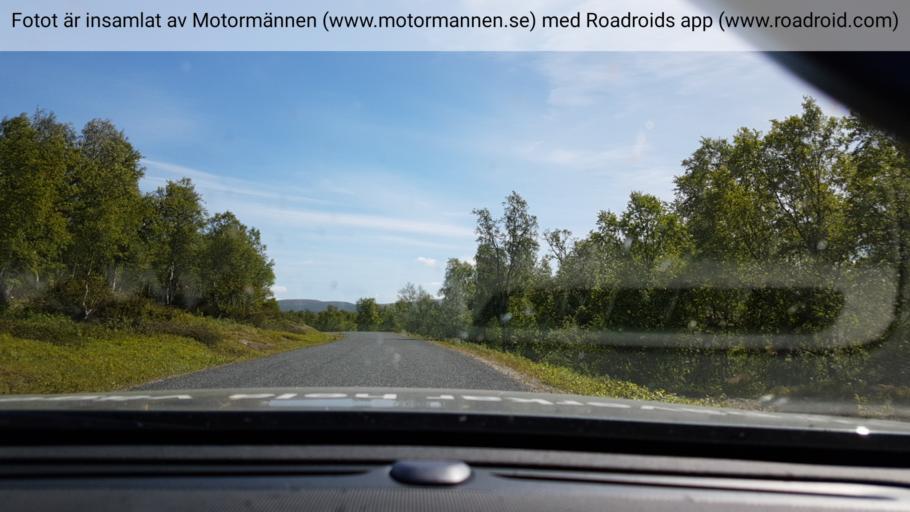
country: NO
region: Nordland
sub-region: Hattfjelldal
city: Hattfjelldal
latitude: 65.4169
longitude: 14.7413
